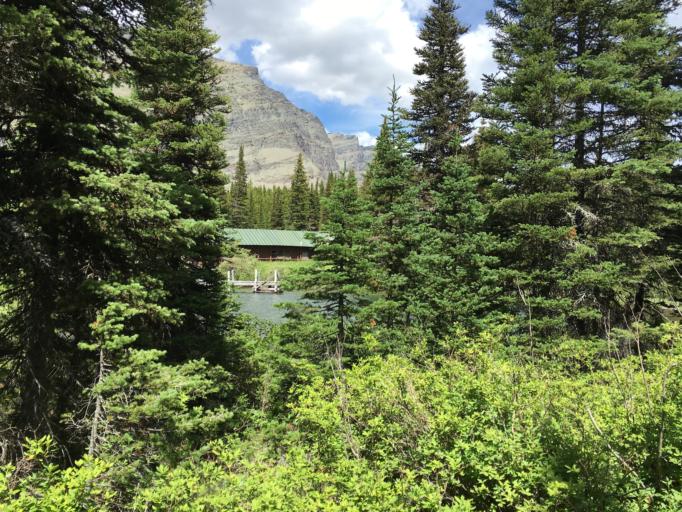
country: CA
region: Alberta
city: Cardston
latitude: 48.7904
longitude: -113.6614
